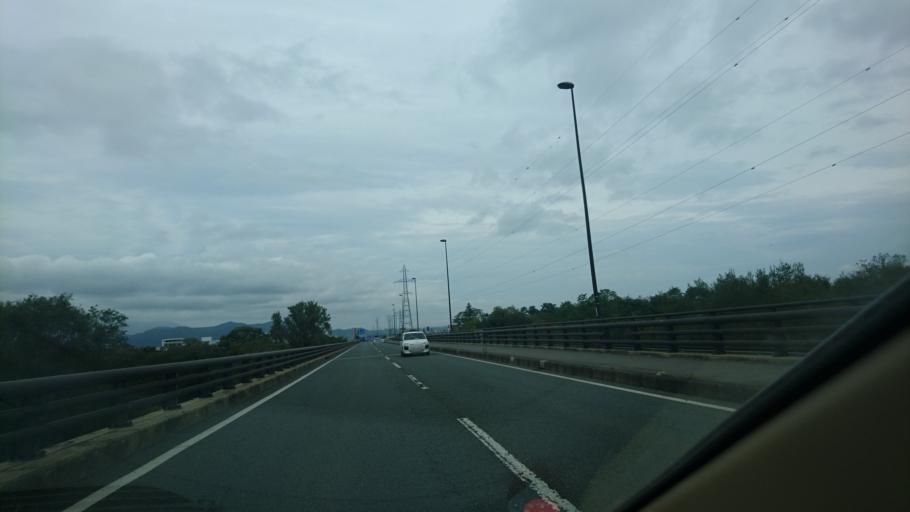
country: JP
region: Iwate
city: Morioka-shi
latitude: 39.7050
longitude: 141.1019
